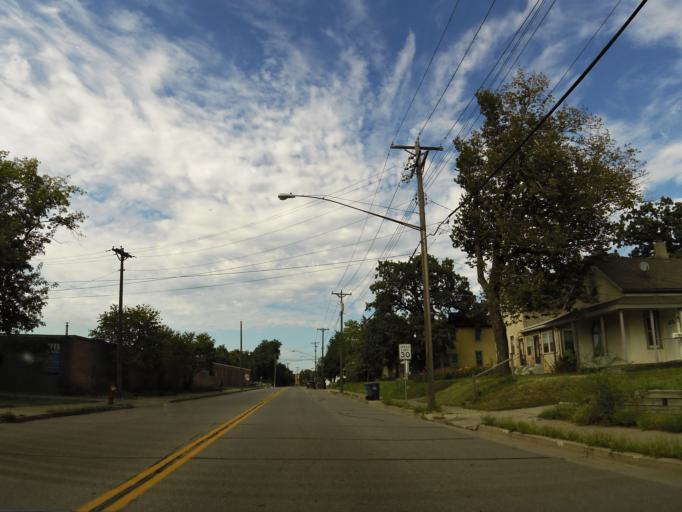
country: US
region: Minnesota
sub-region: Hennepin County
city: Minneapolis
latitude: 45.0045
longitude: -93.2714
